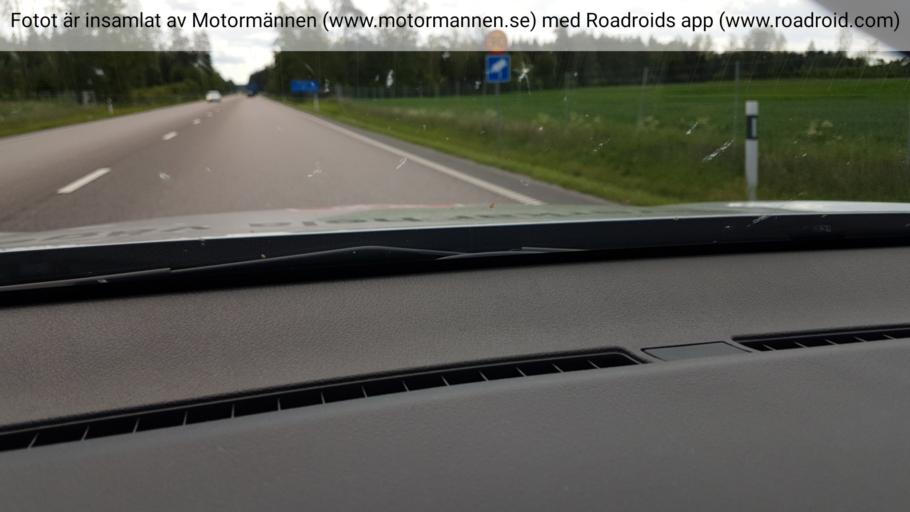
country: SE
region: Vaestra Goetaland
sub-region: Lidkopings Kommun
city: Vinninga
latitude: 58.4667
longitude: 13.2175
